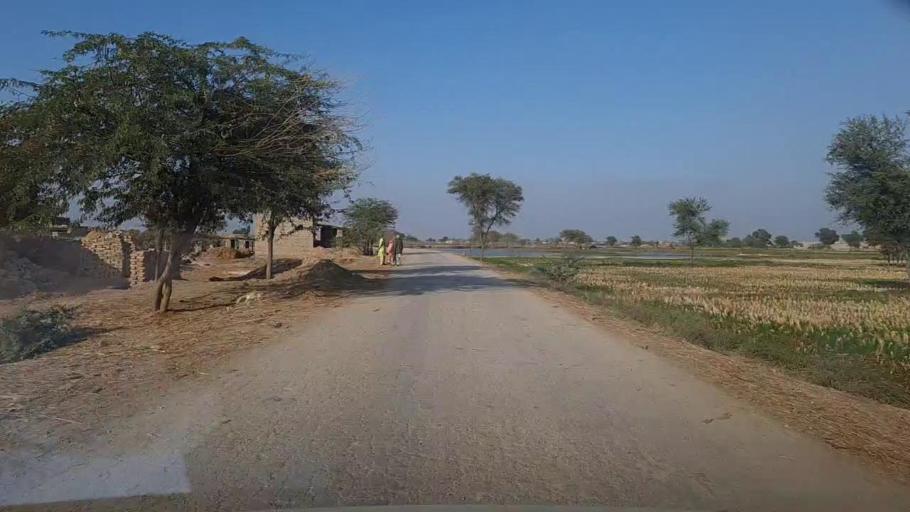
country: PK
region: Sindh
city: Phulji
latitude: 26.8606
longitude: 67.7946
